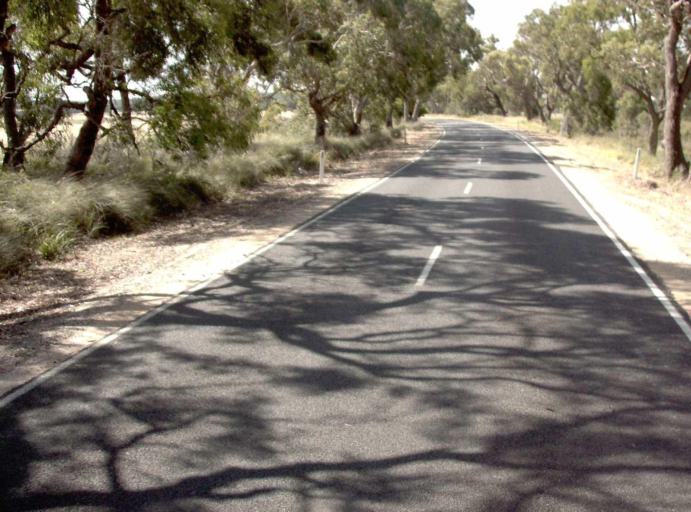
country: AU
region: Victoria
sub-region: Wellington
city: Sale
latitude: -38.2823
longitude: 147.1528
